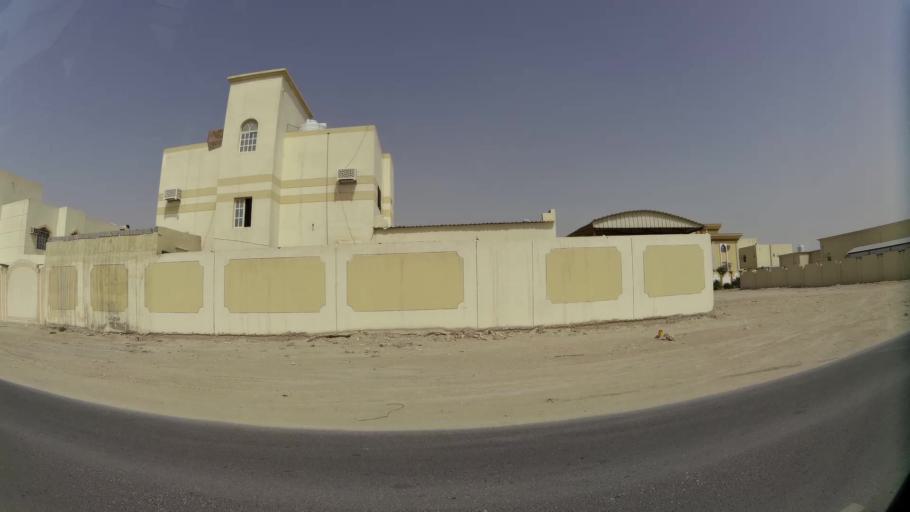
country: QA
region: Baladiyat ar Rayyan
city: Ar Rayyan
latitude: 25.2443
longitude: 51.3634
